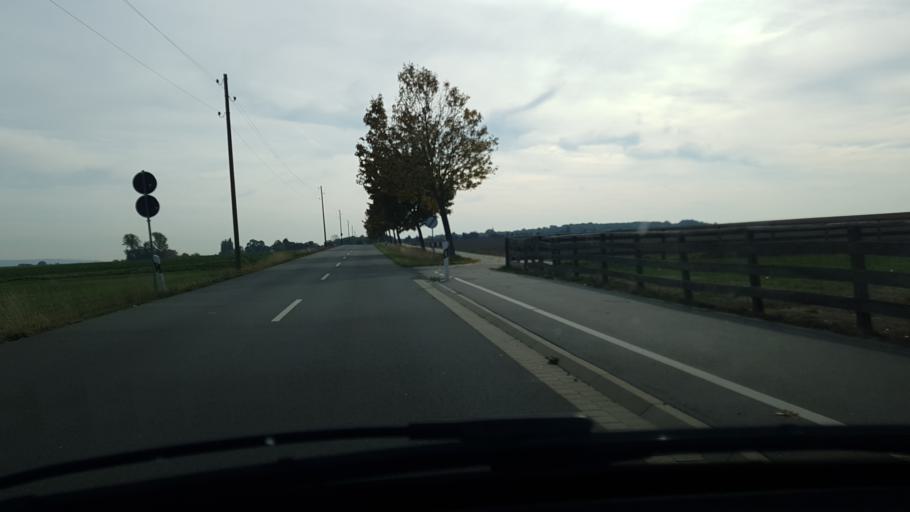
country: DE
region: Lower Saxony
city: Lehre
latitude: 52.3612
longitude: 10.6726
